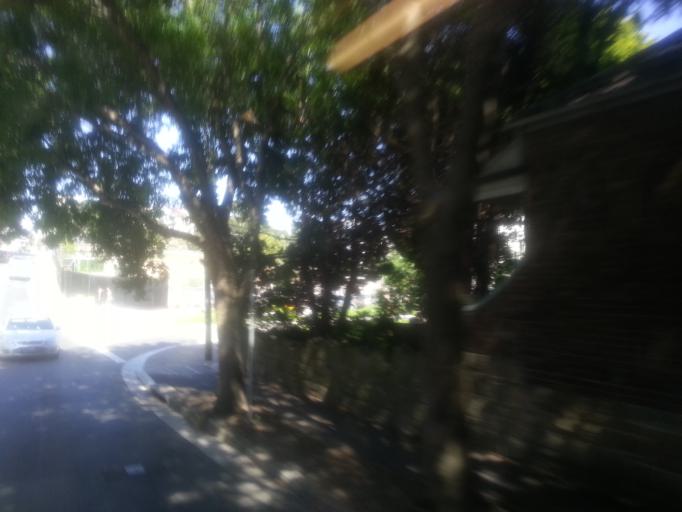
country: AU
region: New South Wales
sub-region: Marrickville
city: Camperdown
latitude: -33.8798
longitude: 151.1808
